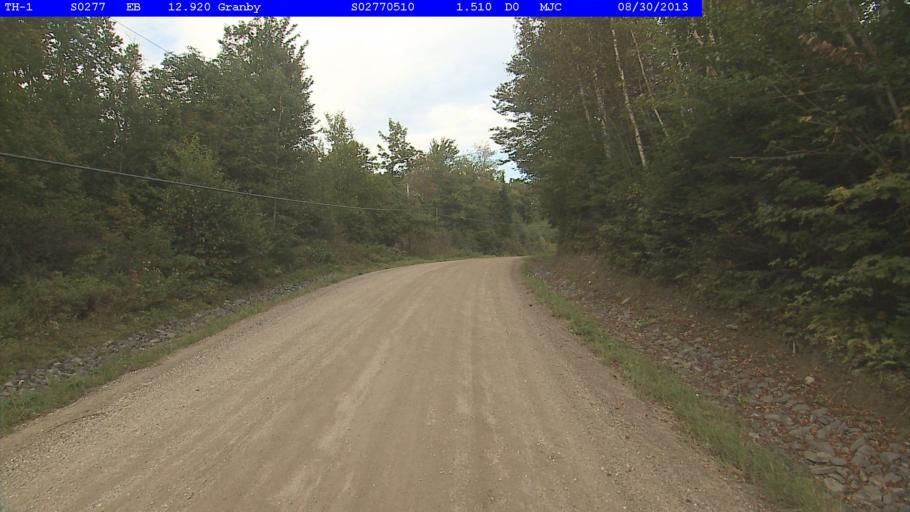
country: US
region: Vermont
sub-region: Essex County
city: Guildhall
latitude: 44.5747
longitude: -71.7350
